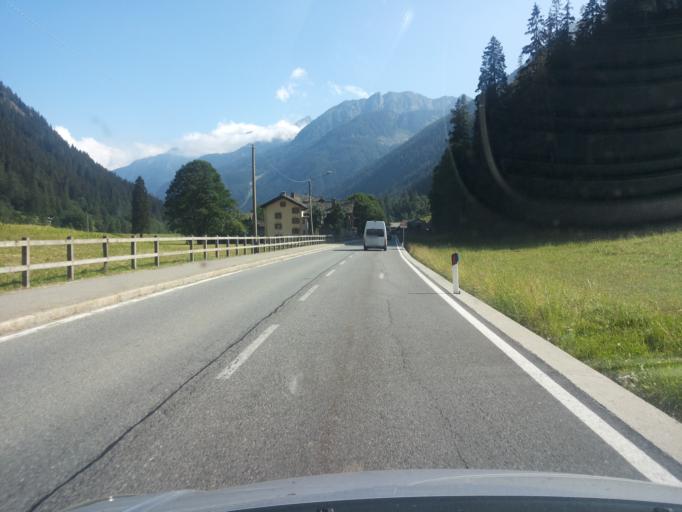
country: IT
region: Aosta Valley
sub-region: Valle d'Aosta
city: Gressoney-Saint-Jean
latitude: 45.7902
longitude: 7.8224
